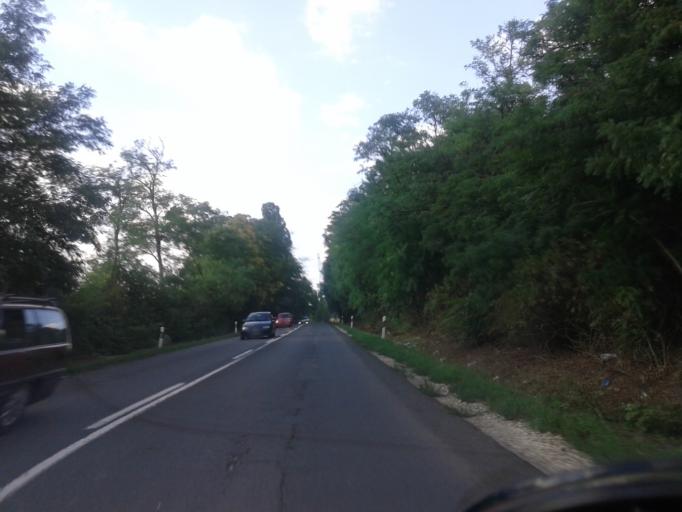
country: HU
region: Pest
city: Kiskunlachaza
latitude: 47.2389
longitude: 19.0207
